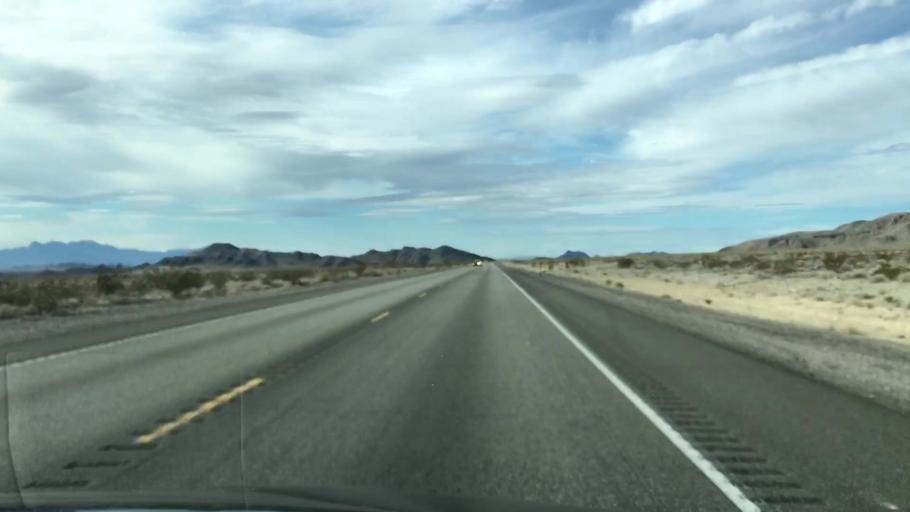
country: US
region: Nevada
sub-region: Nye County
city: Pahrump
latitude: 36.5716
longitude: -116.1709
